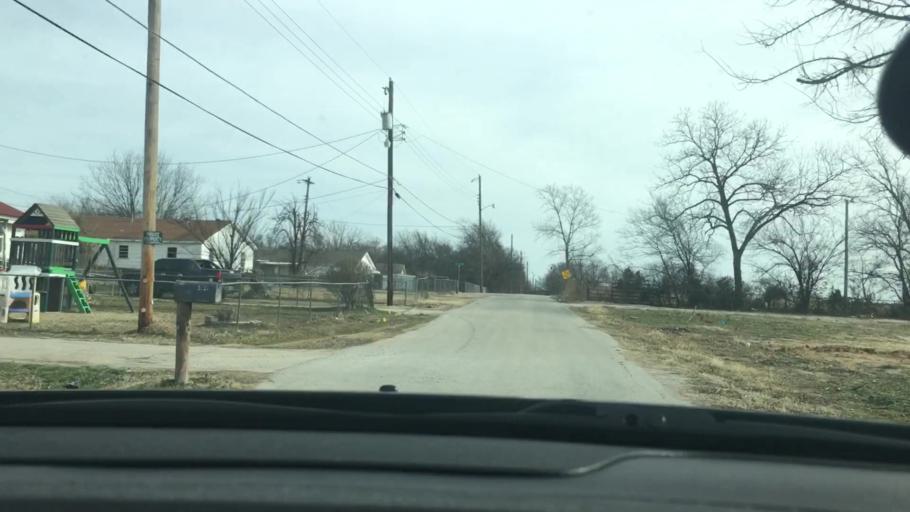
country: US
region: Oklahoma
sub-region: Carter County
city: Ardmore
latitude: 34.1729
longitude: -97.1065
